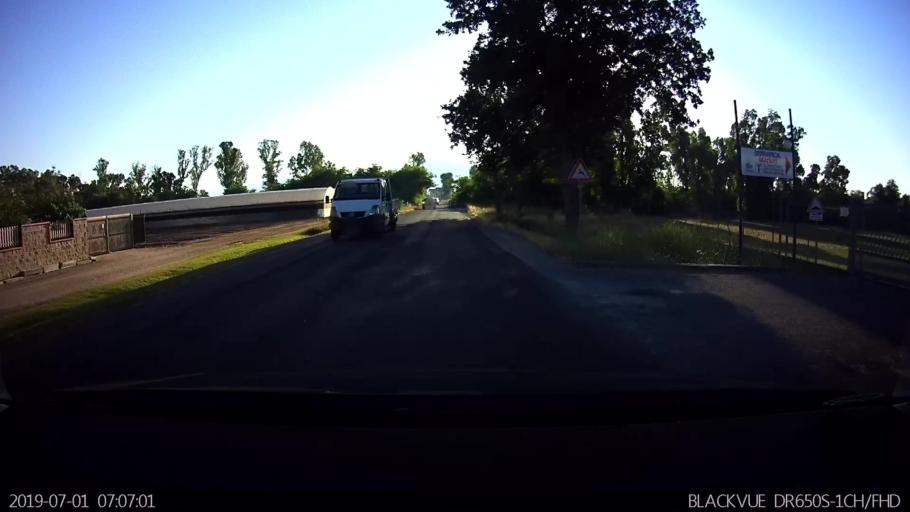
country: IT
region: Latium
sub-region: Provincia di Latina
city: Borgo Hermada
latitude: 41.2867
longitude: 13.1353
